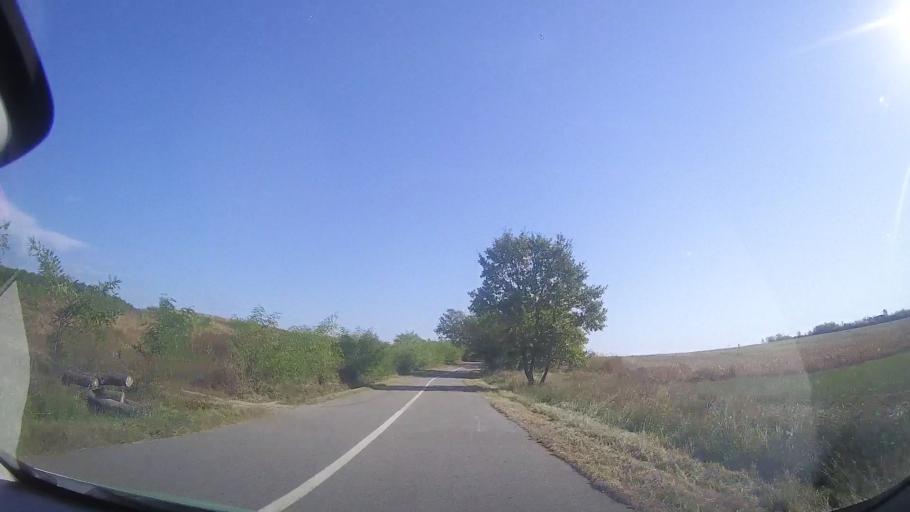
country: RO
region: Timis
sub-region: Comuna Ghizela
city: Ghizela
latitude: 45.8281
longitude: 21.7457
